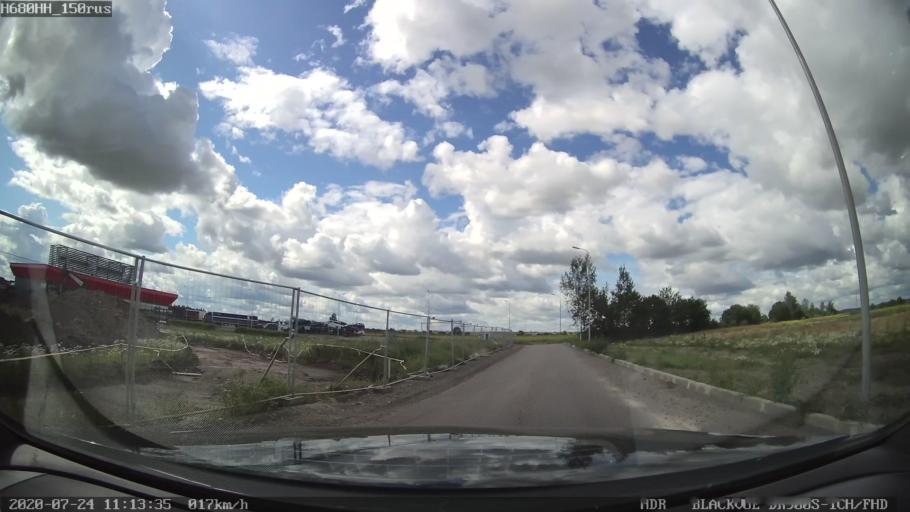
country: RU
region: Leningrad
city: Fedorovskoye
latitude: 59.7020
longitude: 30.5513
